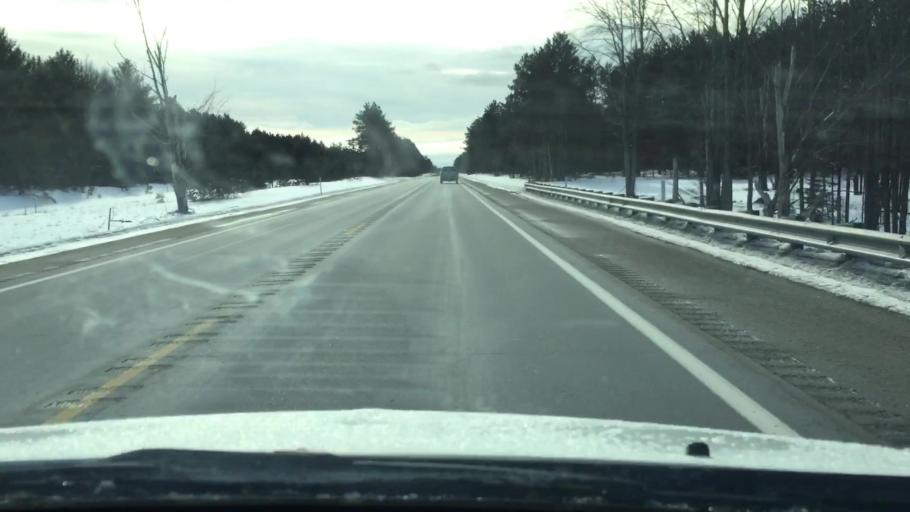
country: US
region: Michigan
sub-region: Kalkaska County
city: Kalkaska
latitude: 44.6894
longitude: -85.2173
